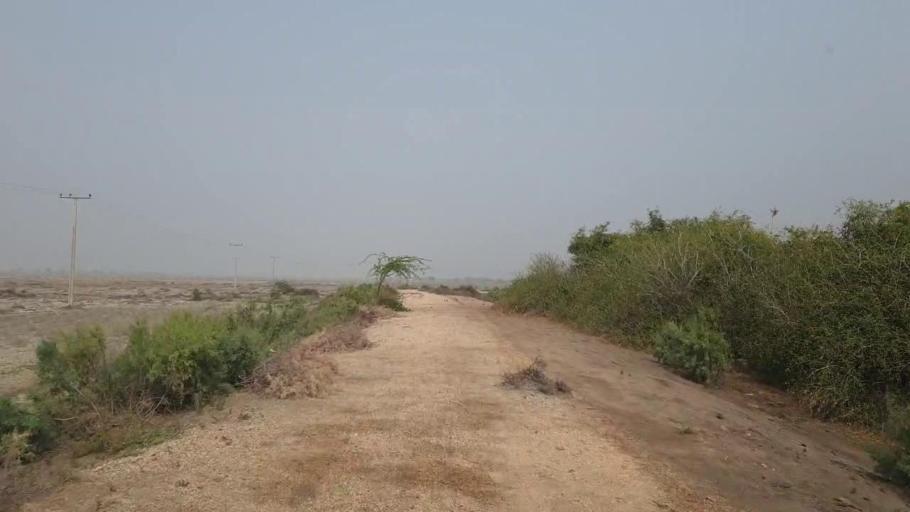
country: PK
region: Sindh
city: Kario
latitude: 24.6669
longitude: 68.6468
